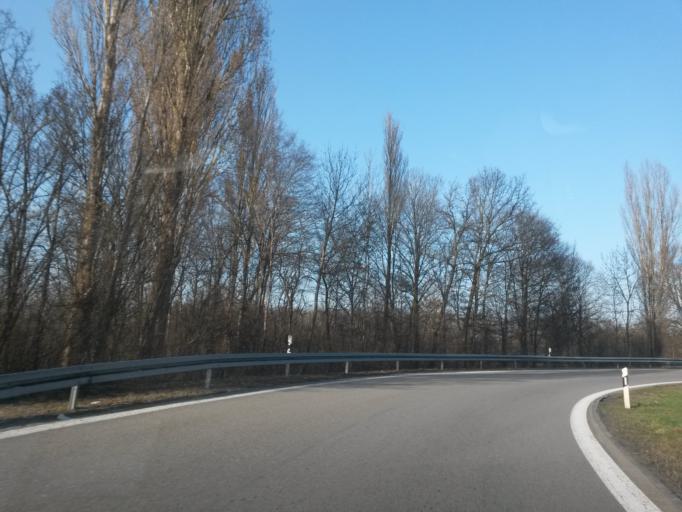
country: DE
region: Bavaria
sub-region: Upper Bavaria
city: Ingolstadt
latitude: 48.7513
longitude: 11.4583
